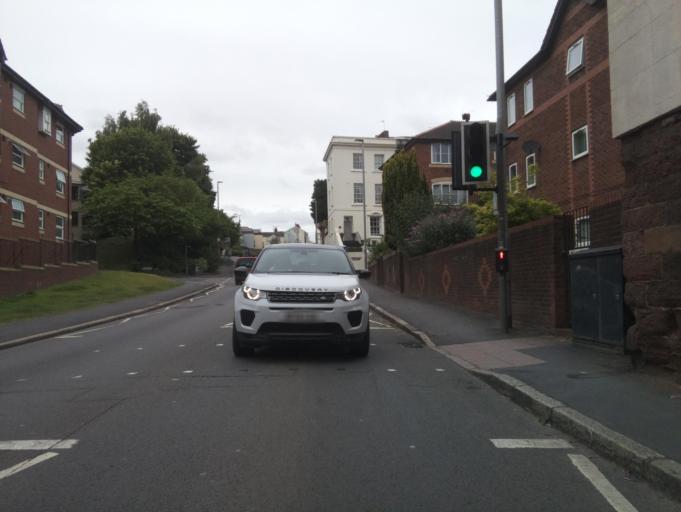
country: GB
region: England
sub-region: Devon
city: Exeter
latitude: 50.7180
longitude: -3.5259
